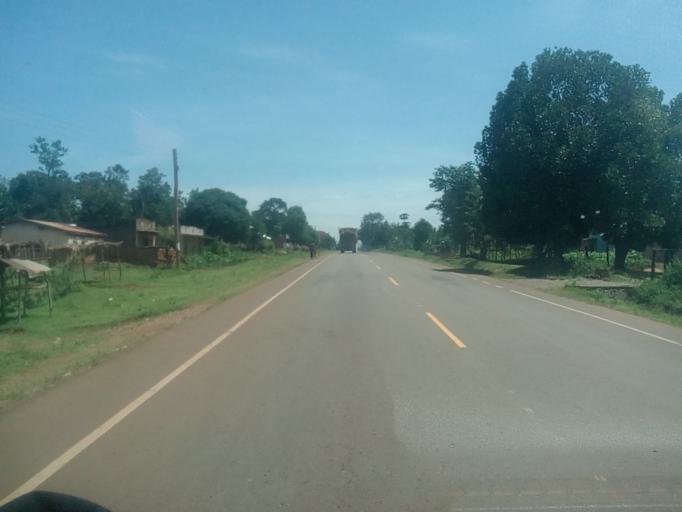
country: UG
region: Eastern Region
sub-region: Kamuli District
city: Kamuli
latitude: 0.9217
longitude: 33.1086
